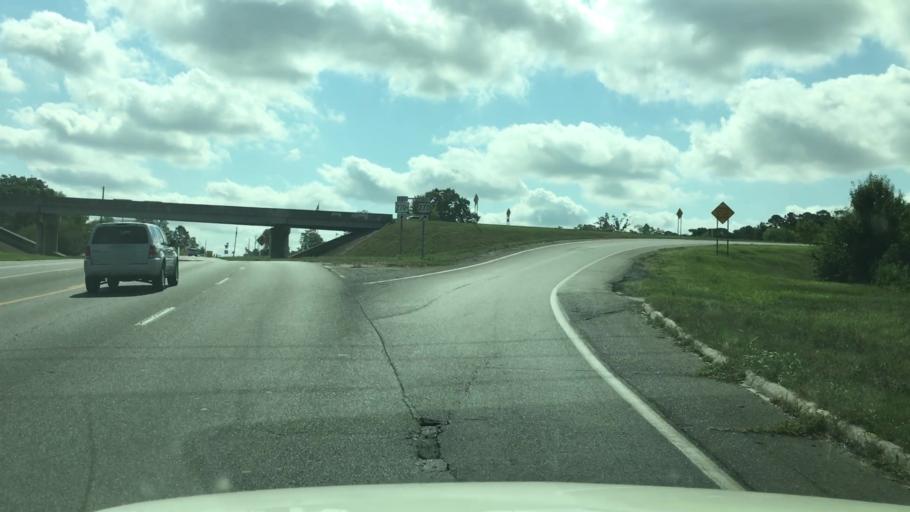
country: US
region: Arkansas
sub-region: Garland County
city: Piney
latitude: 34.4925
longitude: -93.1133
